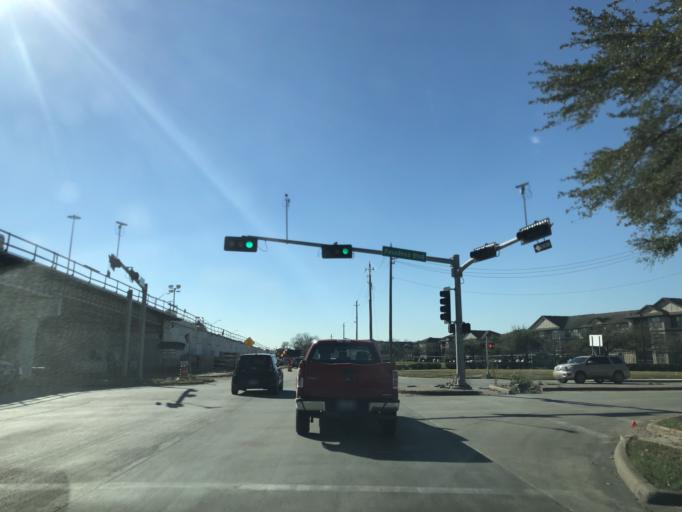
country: US
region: Texas
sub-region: Harris County
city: Deer Park
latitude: 29.6818
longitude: -95.1557
